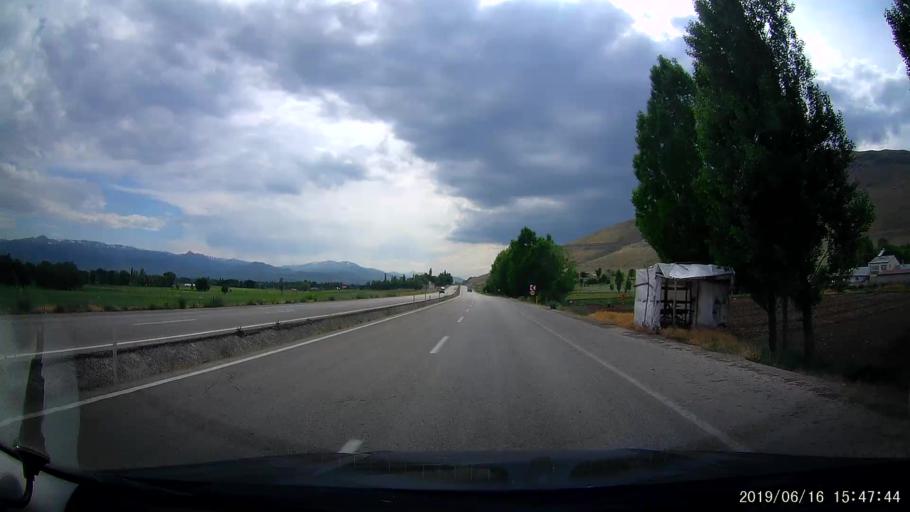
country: TR
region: Erzurum
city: Pasinler
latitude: 39.9872
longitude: 41.7144
